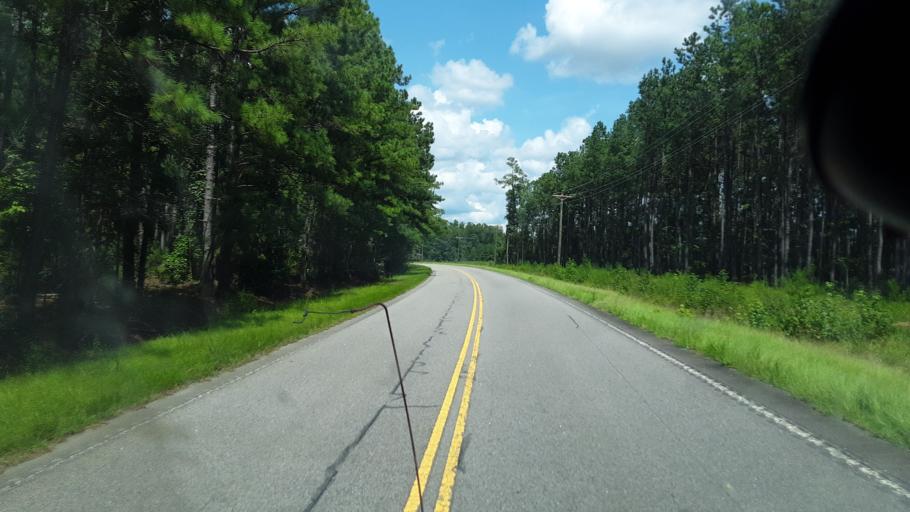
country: US
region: South Carolina
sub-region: Williamsburg County
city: Andrews
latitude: 33.5185
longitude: -79.4949
